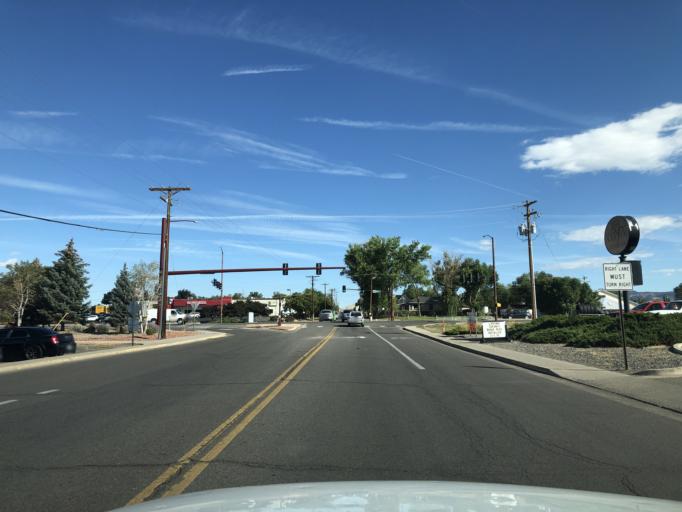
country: US
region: Colorado
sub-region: Montrose County
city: Montrose
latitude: 38.4875
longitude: -107.8571
